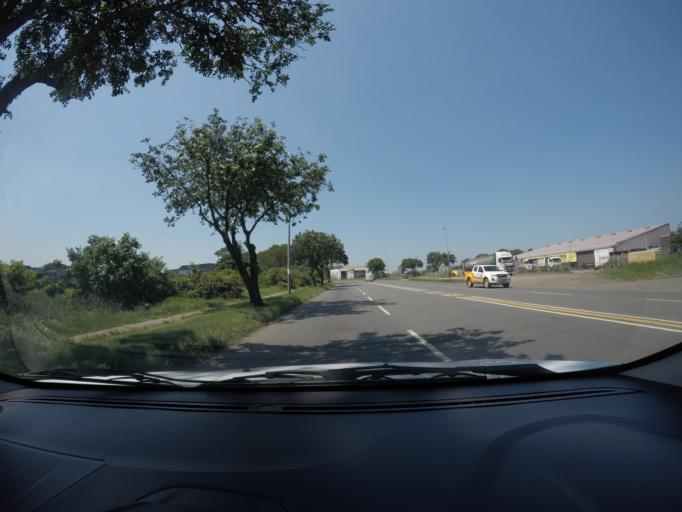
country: ZA
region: KwaZulu-Natal
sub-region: uThungulu District Municipality
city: Richards Bay
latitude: -28.7571
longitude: 32.0250
